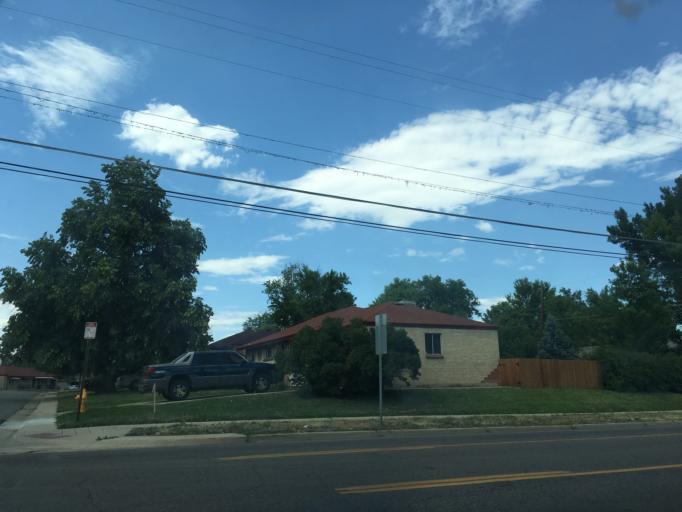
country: US
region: Colorado
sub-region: Jefferson County
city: Lakewood
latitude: 39.6894
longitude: -105.0490
